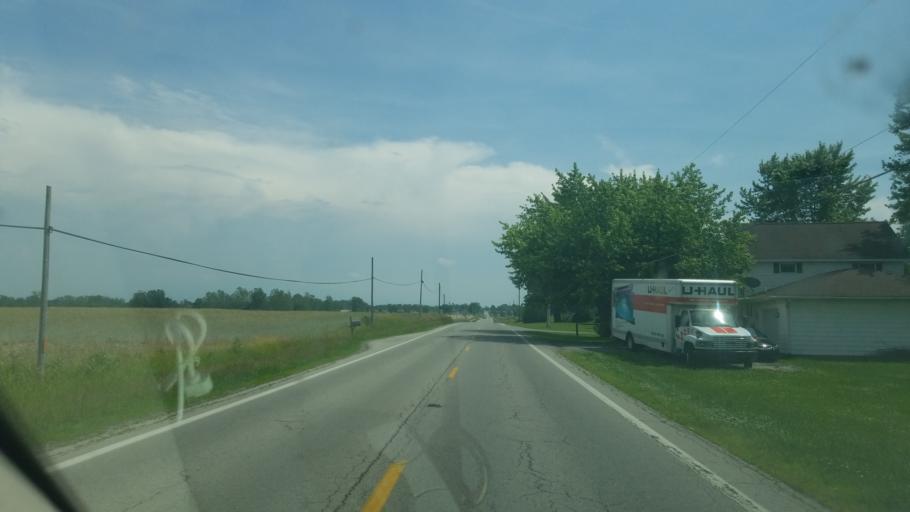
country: US
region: Ohio
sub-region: Logan County
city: Northwood
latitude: 40.5003
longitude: -83.7431
